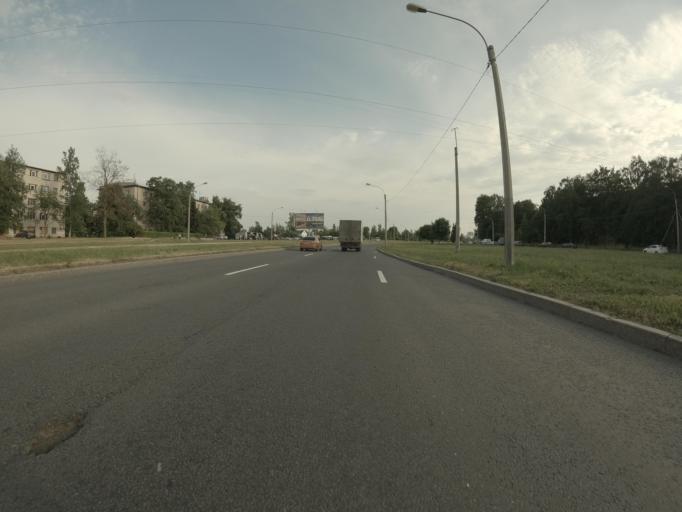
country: RU
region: Leningrad
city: Rybatskoye
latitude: 59.8832
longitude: 30.4883
